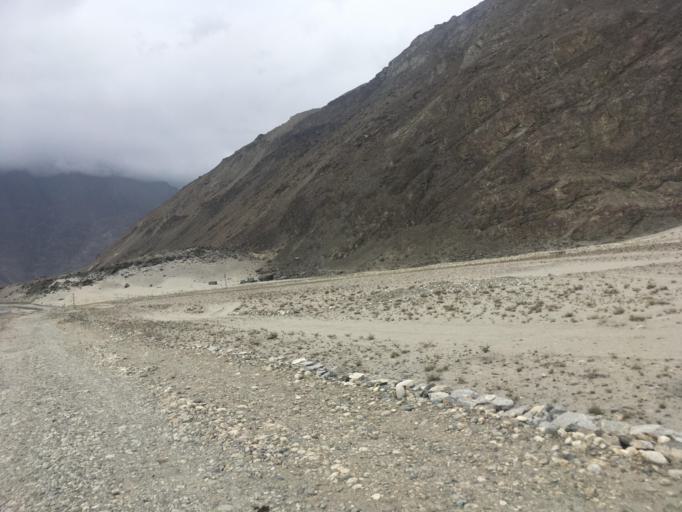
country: PK
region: Gilgit-Baltistan
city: Skardu
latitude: 35.3129
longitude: 75.6579
